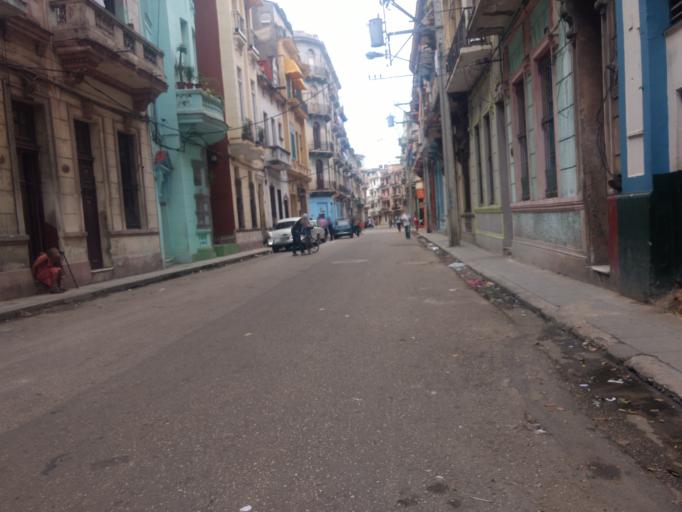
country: CU
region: La Habana
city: Havana
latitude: 23.1392
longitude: -82.3759
